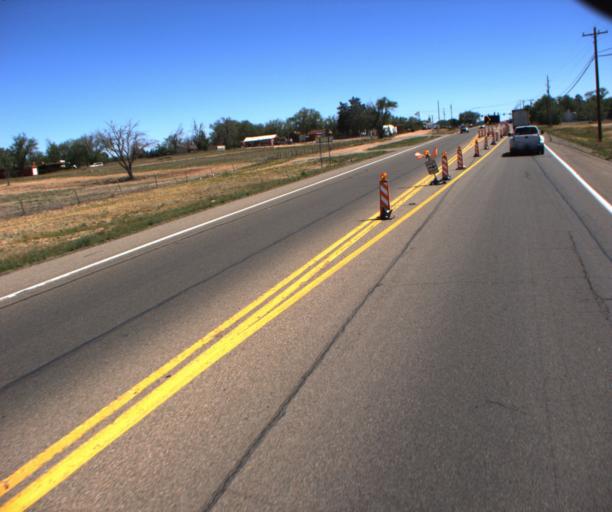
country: US
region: Arizona
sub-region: Yavapai County
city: Chino Valley
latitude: 34.7781
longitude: -112.4527
